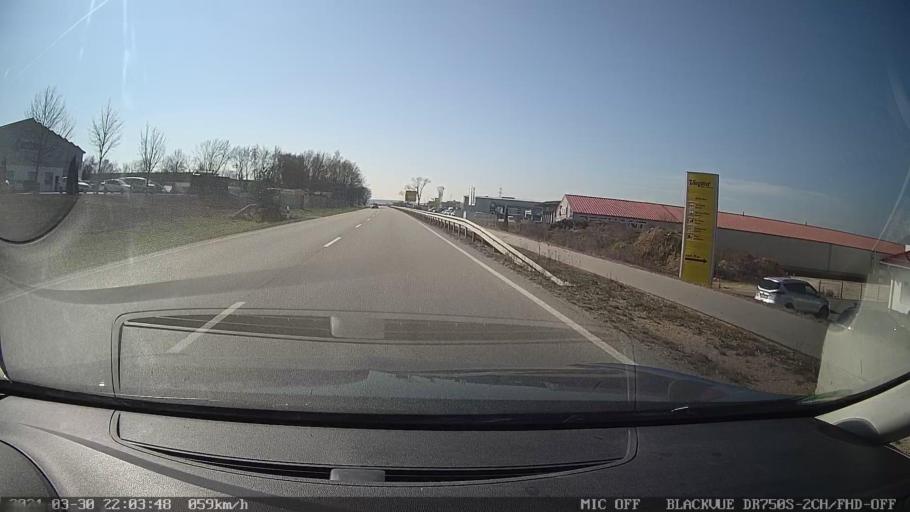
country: DE
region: Bavaria
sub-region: Upper Palatinate
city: Regenstauf
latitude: 49.1115
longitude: 12.1248
